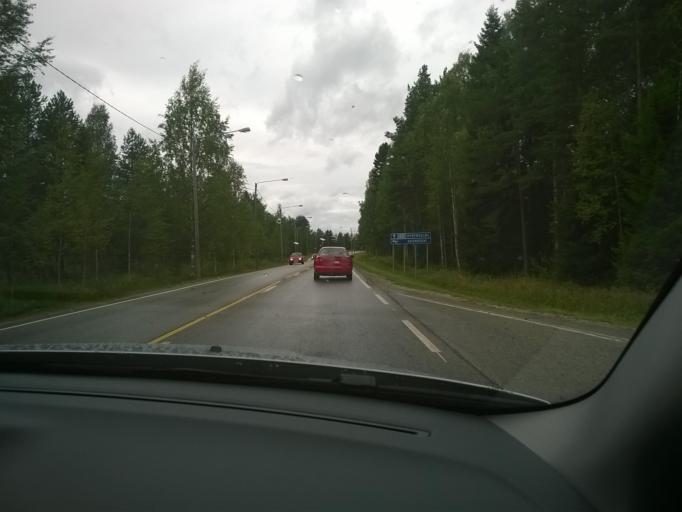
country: FI
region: Kainuu
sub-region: Kehys-Kainuu
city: Kuhmo
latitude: 64.1306
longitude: 29.4791
